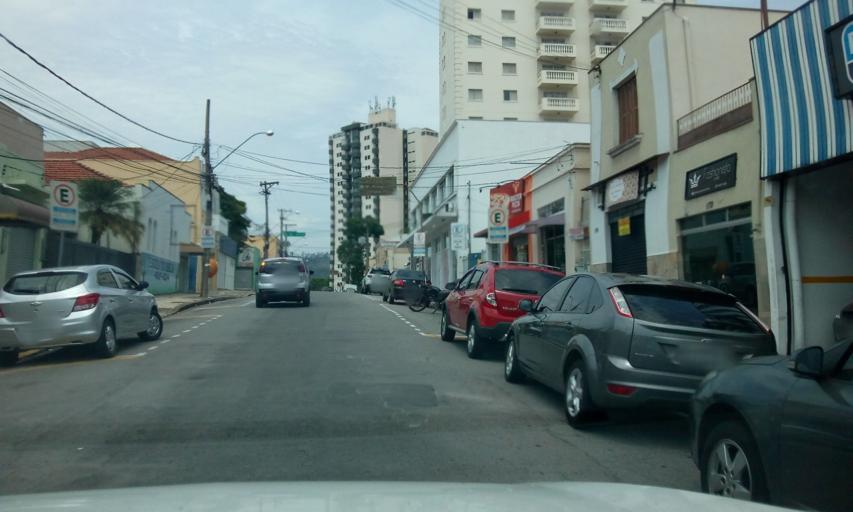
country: BR
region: Sao Paulo
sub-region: Jundiai
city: Jundiai
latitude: -23.1979
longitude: -46.8770
